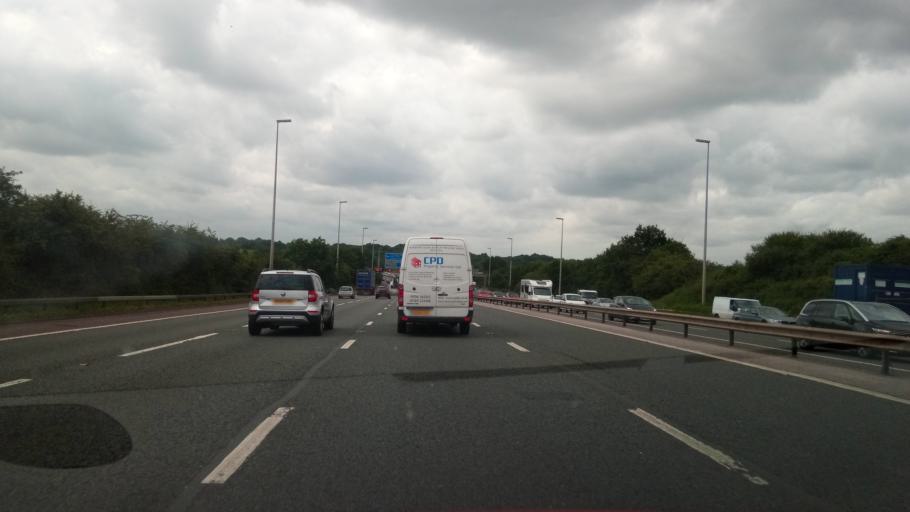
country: GB
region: England
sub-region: Lancashire
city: Clayton-le-Woods
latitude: 53.7490
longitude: -2.6457
